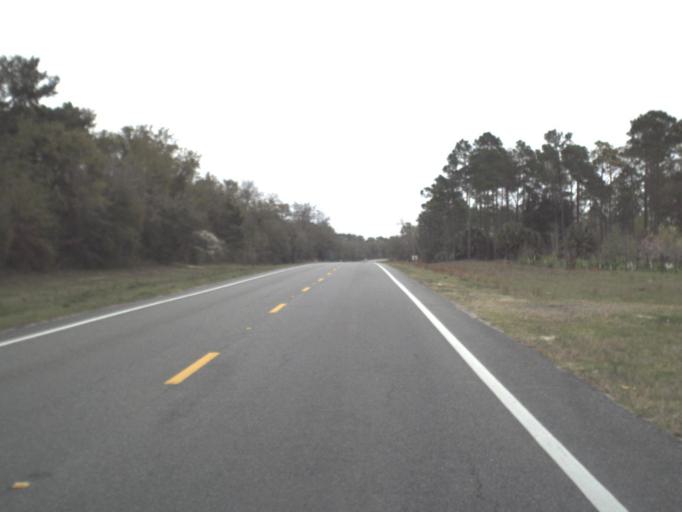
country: US
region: Florida
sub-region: Wakulla County
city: Crawfordville
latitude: 30.1193
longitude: -84.3706
